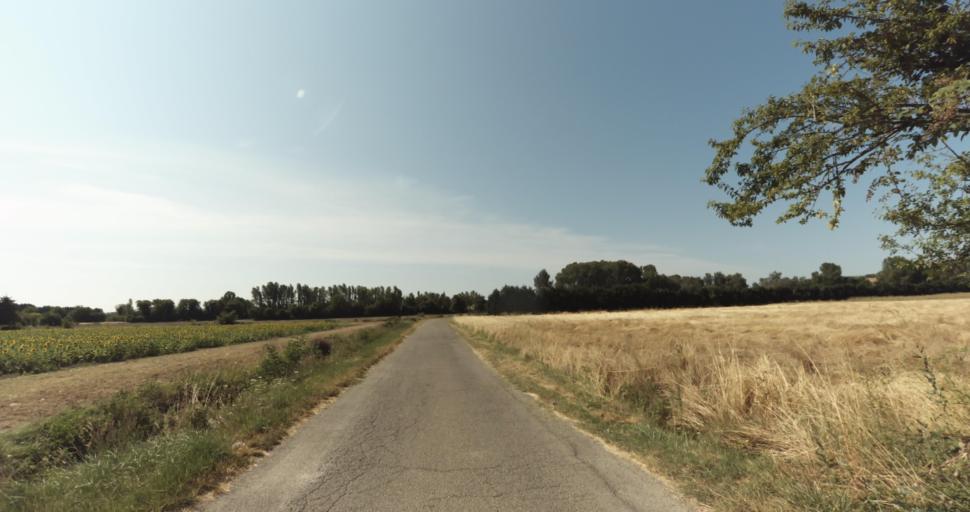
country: FR
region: Provence-Alpes-Cote d'Azur
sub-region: Departement du Vaucluse
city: Althen-des-Paluds
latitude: 44.0090
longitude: 4.9737
